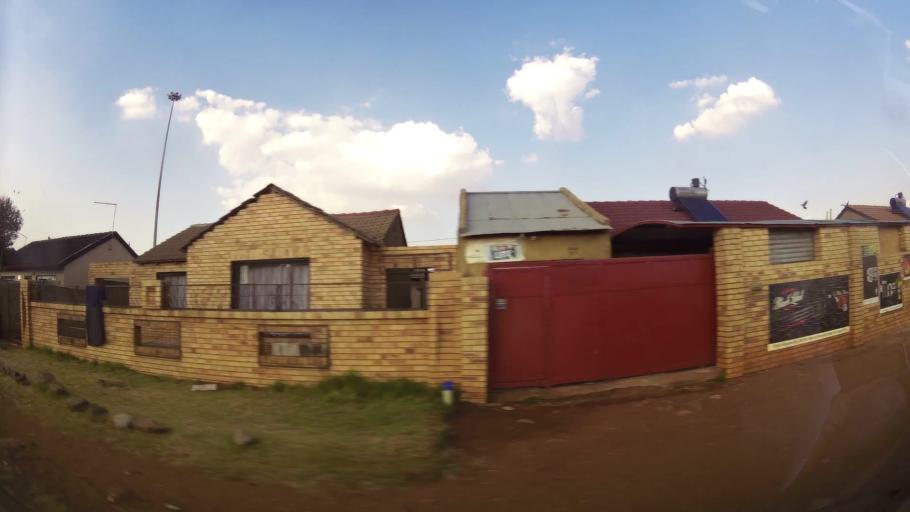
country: ZA
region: Gauteng
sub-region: Ekurhuleni Metropolitan Municipality
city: Germiston
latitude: -26.3676
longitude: 28.2294
